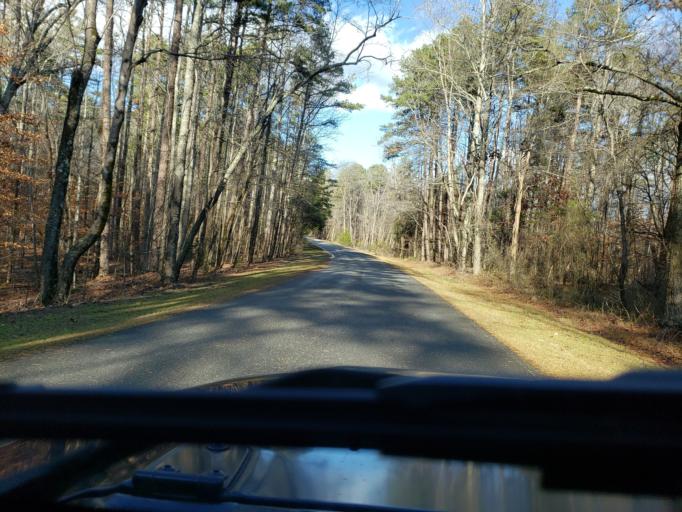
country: US
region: North Carolina
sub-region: Cleveland County
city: Kings Mountain
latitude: 35.1558
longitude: -81.3302
